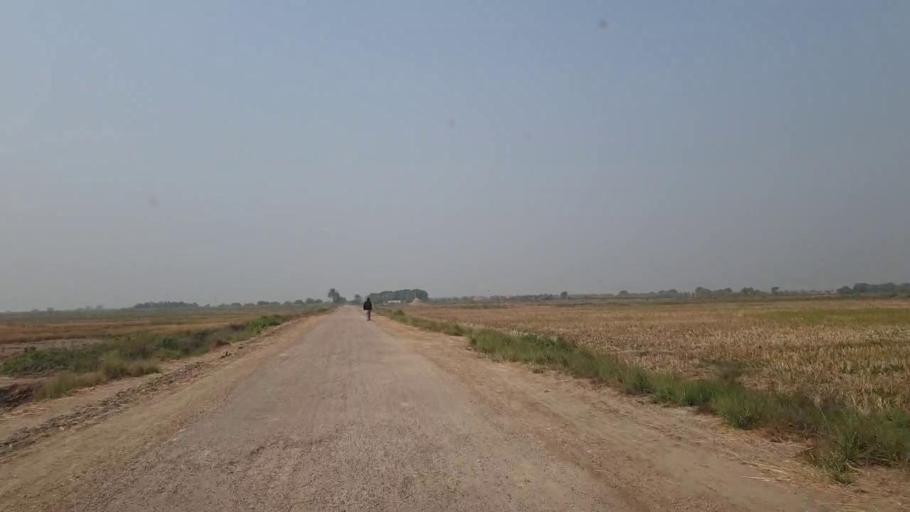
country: PK
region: Sindh
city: Matli
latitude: 25.1229
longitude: 68.6499
